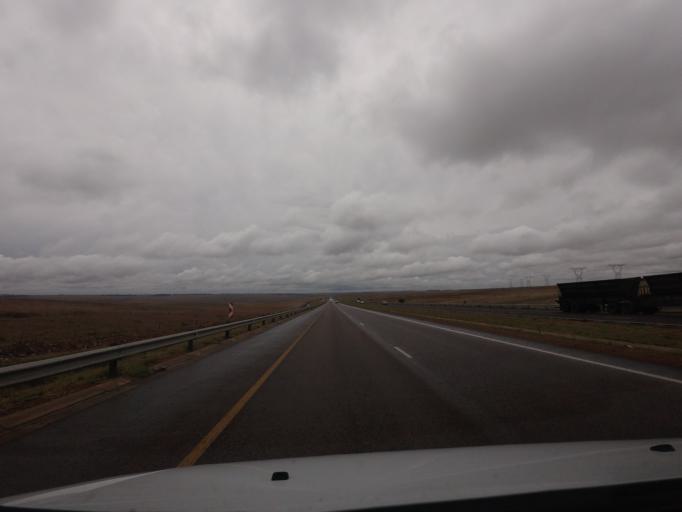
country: ZA
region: Mpumalanga
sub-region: Nkangala District Municipality
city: Middelburg
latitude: -25.8242
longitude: 29.5624
